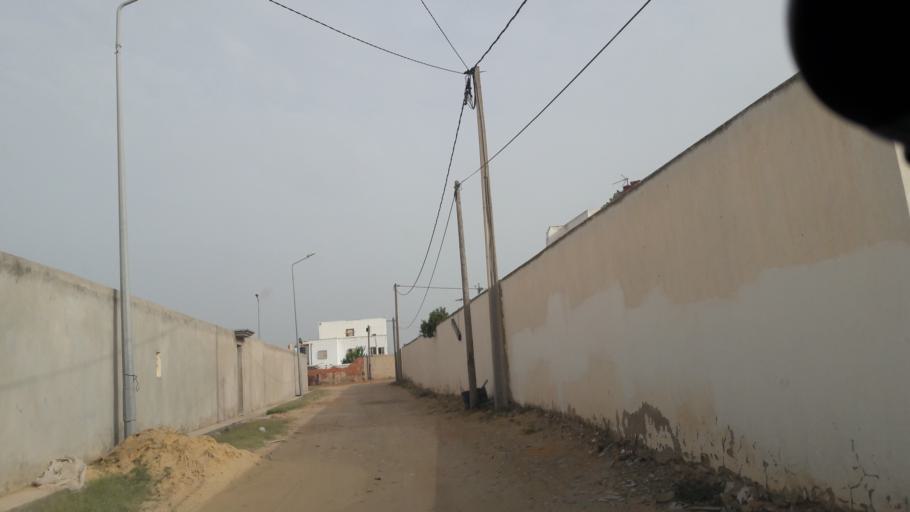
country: TN
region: Safaqis
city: Al Qarmadah
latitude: 34.7800
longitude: 10.7708
